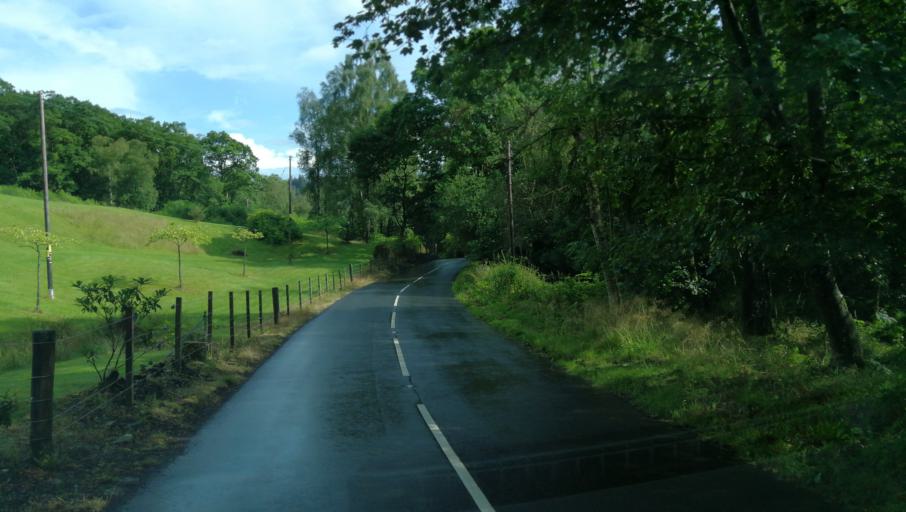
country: GB
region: Scotland
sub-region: Stirling
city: Balfron
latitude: 56.2294
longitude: -4.3931
